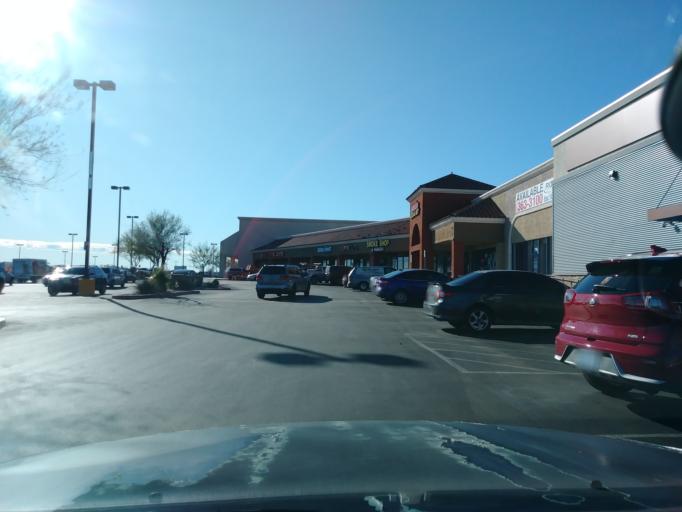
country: US
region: Nevada
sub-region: Clark County
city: Spring Valley
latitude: 36.1642
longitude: -115.2456
